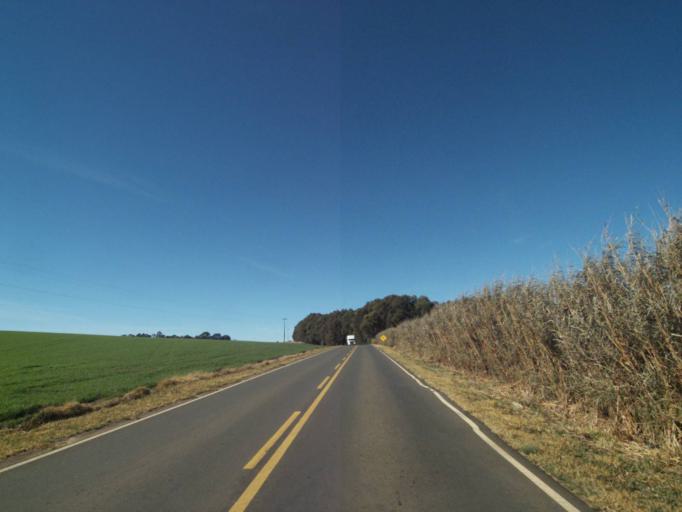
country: BR
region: Parana
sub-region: Tibagi
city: Tibagi
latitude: -24.5790
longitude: -50.2723
